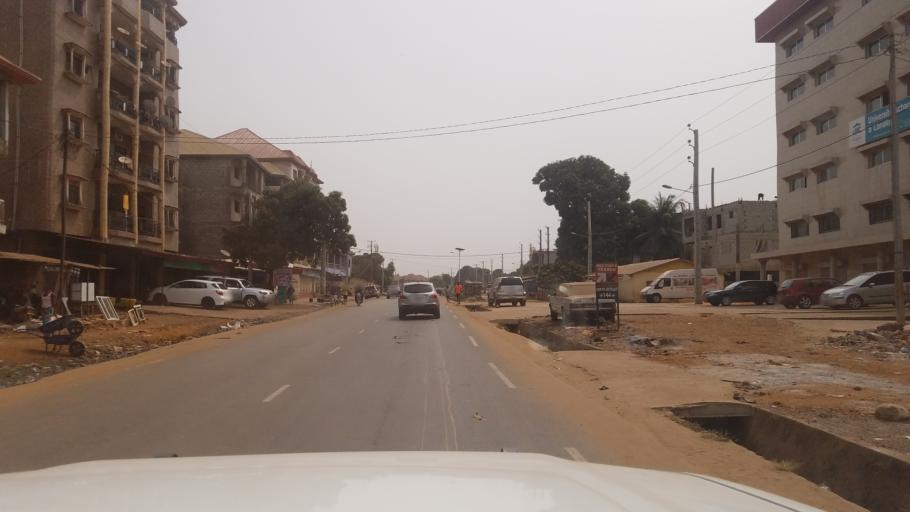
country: GN
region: Kindia
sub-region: Prefecture de Dubreka
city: Dubreka
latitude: 9.6690
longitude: -13.5890
